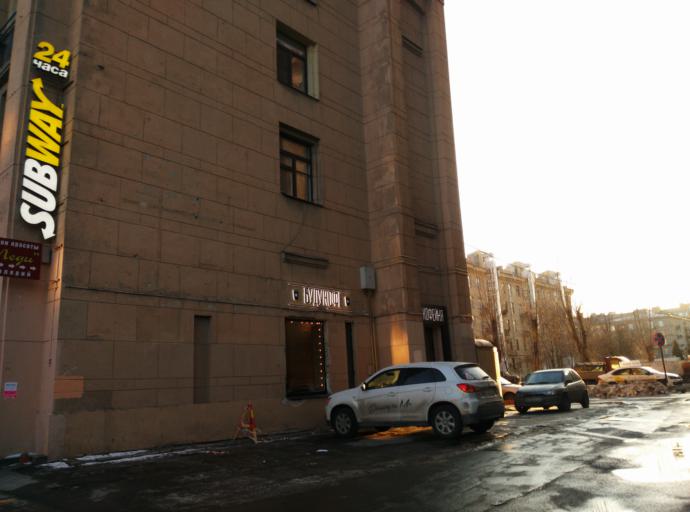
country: RU
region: St.-Petersburg
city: Kupchino
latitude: 59.8779
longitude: 30.3193
